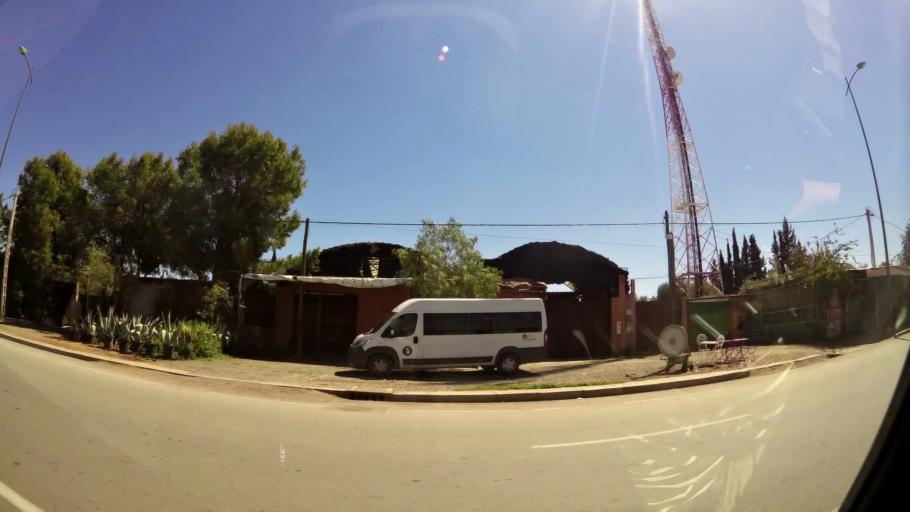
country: MA
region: Marrakech-Tensift-Al Haouz
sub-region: Marrakech
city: Marrakesh
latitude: 31.5712
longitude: -7.9806
